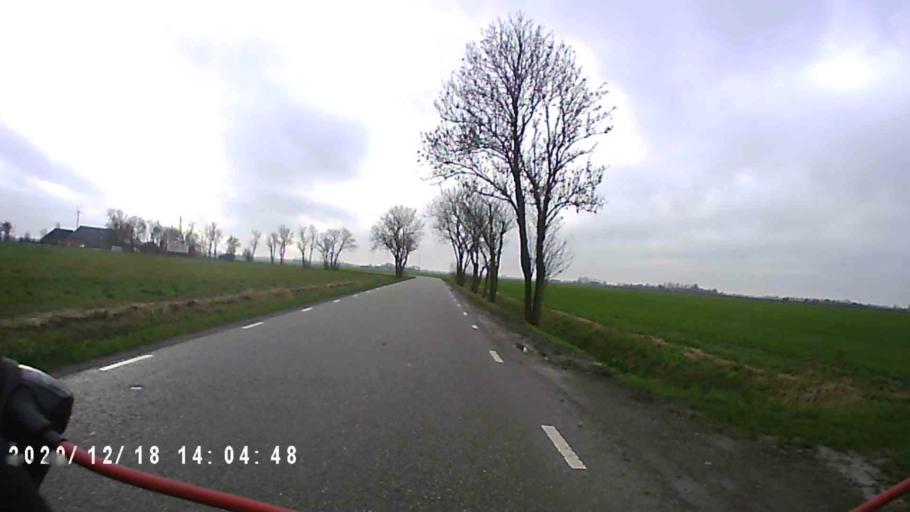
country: NL
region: Groningen
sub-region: Gemeente Bedum
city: Bedum
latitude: 53.2914
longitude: 6.6524
